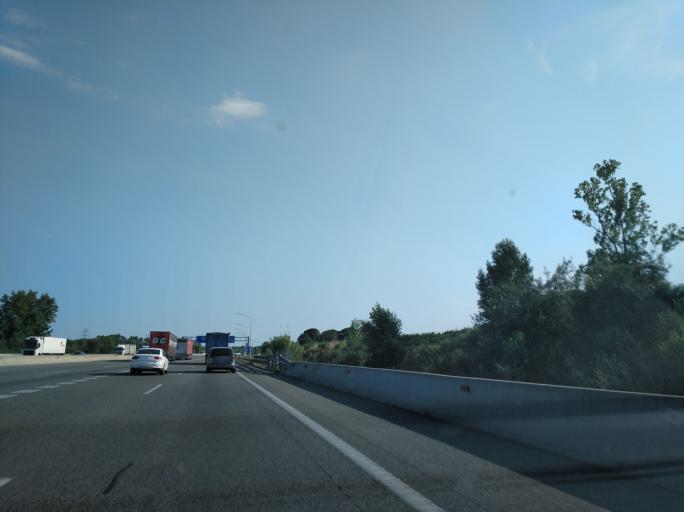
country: ES
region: Catalonia
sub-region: Provincia de Girona
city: Vilablareix
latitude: 41.9409
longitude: 2.7885
